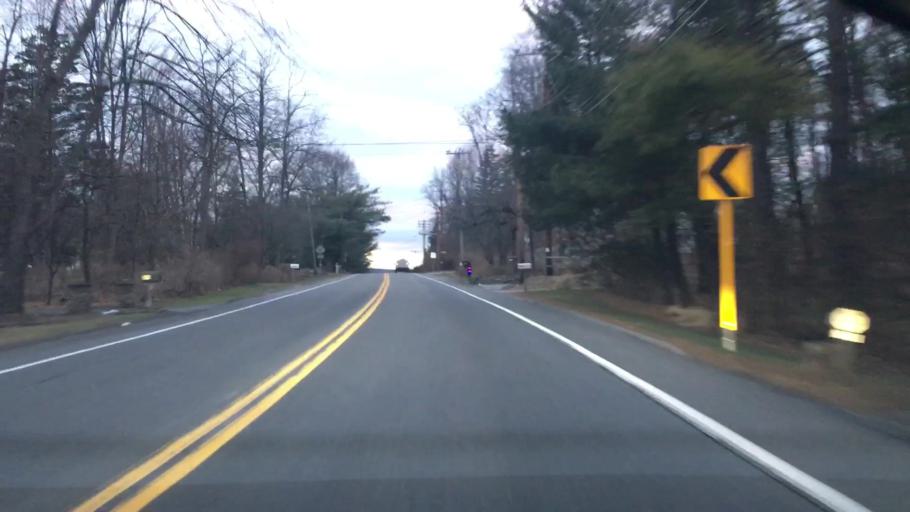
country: US
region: New York
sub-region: Dutchess County
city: Arlington
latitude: 41.6773
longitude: -73.8857
